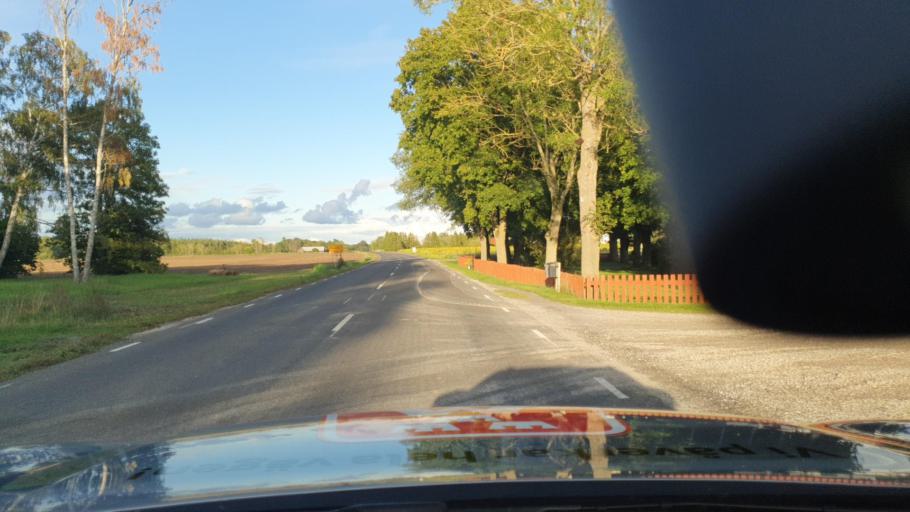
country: SE
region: Gotland
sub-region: Gotland
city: Vibble
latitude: 57.4815
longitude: 18.3237
